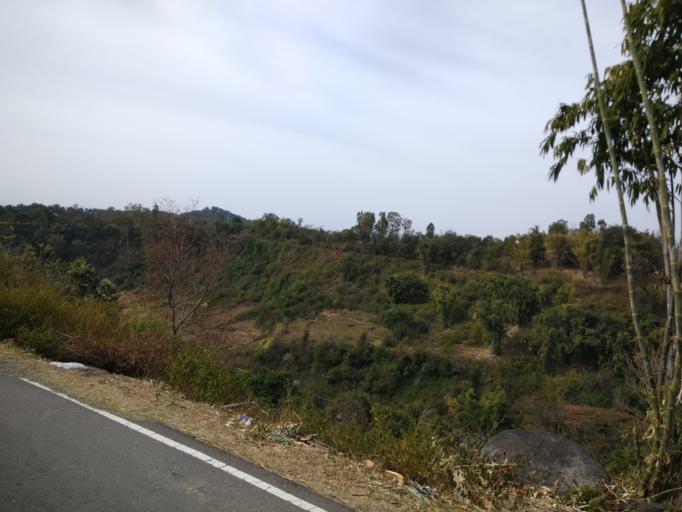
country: IN
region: Himachal Pradesh
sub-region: Kangra
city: Dharmsala
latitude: 32.1592
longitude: 76.4062
